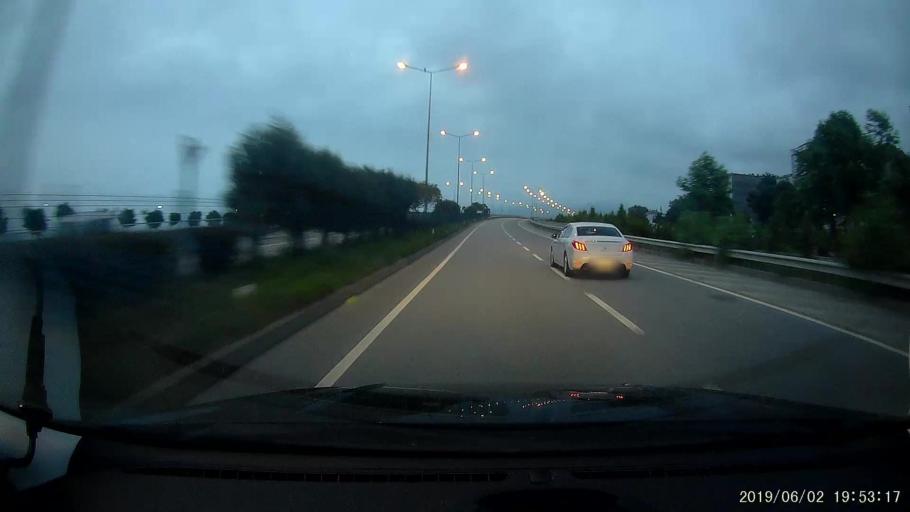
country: TR
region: Trabzon
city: Espiye
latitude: 40.9489
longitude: 38.7025
